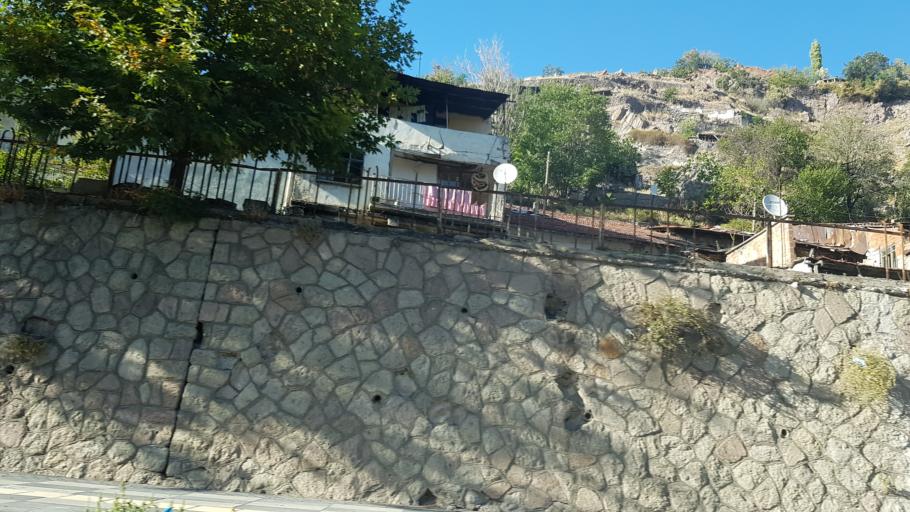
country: TR
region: Ankara
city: Cankaya
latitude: 39.9434
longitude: 32.8657
